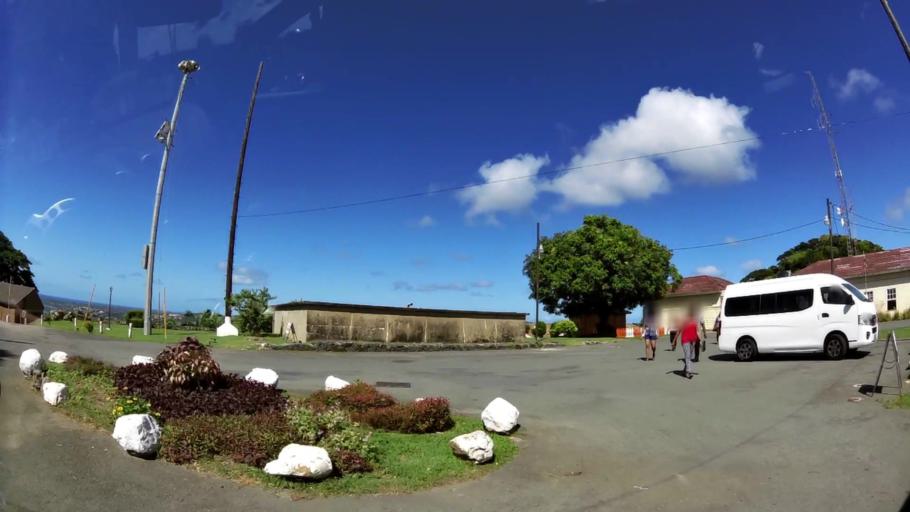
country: TT
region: Tobago
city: Scarborough
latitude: 11.1777
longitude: -60.7268
